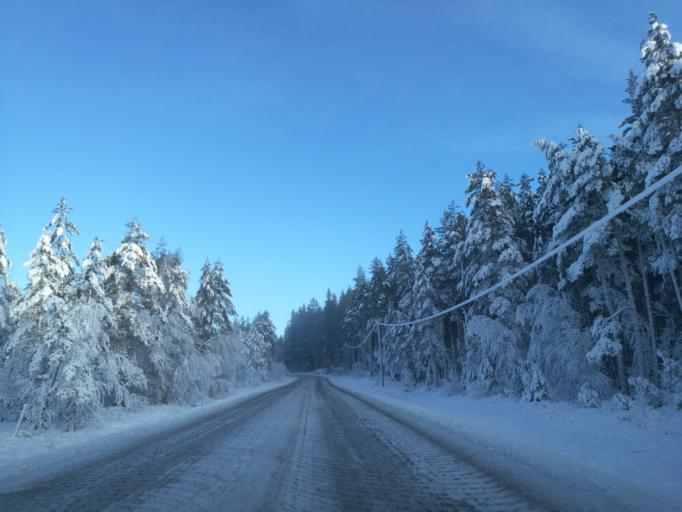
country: NO
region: Hedmark
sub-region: Grue
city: Kirkenaer
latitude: 60.3872
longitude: 12.3625
